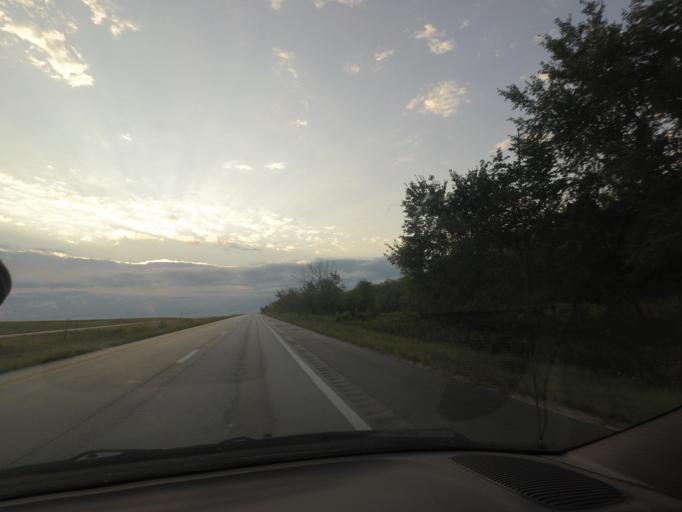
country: US
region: Missouri
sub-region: Shelby County
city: Shelbina
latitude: 39.7225
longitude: -92.1633
